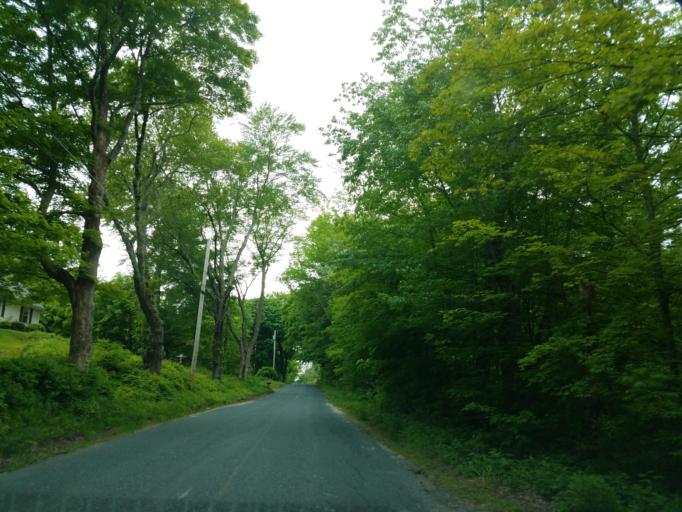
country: US
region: Connecticut
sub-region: Windham County
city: Quinebaug
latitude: 42.0276
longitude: -71.9373
